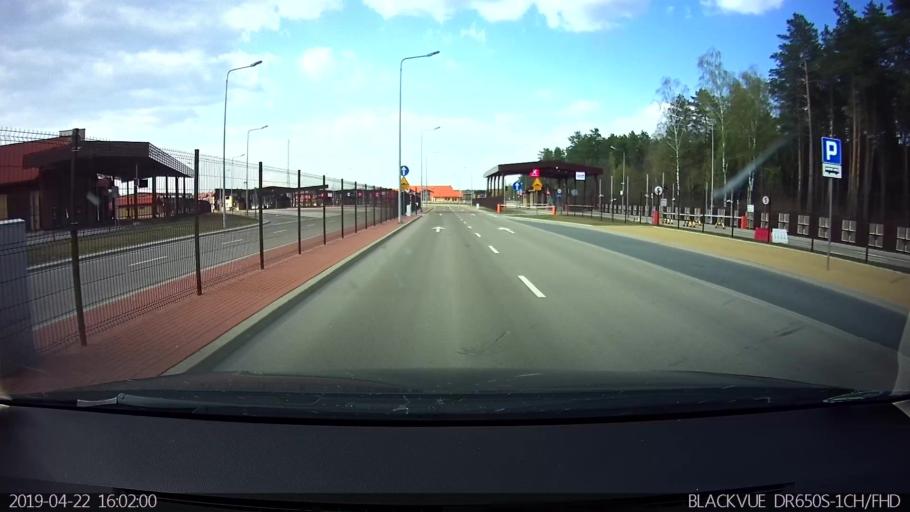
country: PL
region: Podlasie
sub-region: Powiat hajnowski
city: Czeremcha
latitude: 52.4732
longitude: 23.3577
